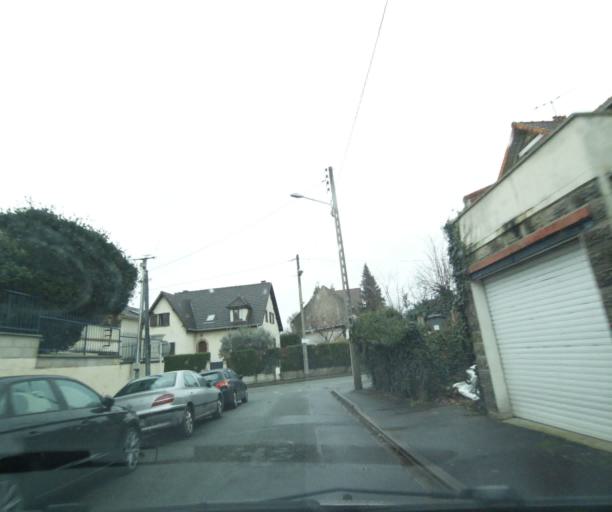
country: FR
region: Ile-de-France
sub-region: Departement du Val-de-Marne
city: Villeneuve-le-Roi
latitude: 48.7394
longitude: 2.4161
